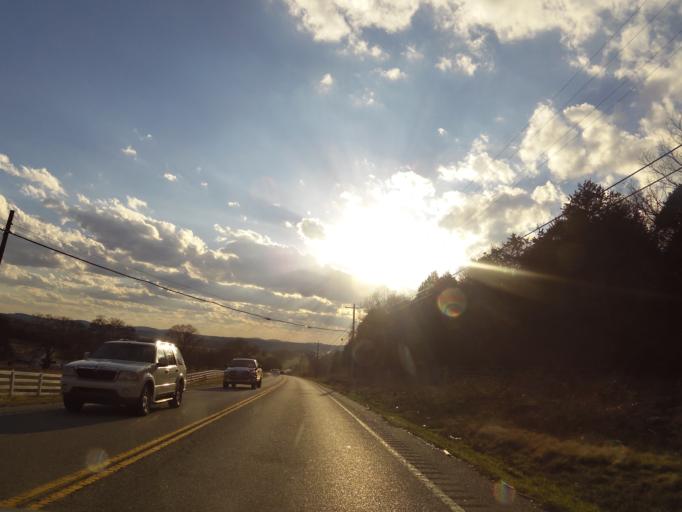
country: US
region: Tennessee
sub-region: Wilson County
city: Lebanon
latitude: 36.2274
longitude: -86.2185
